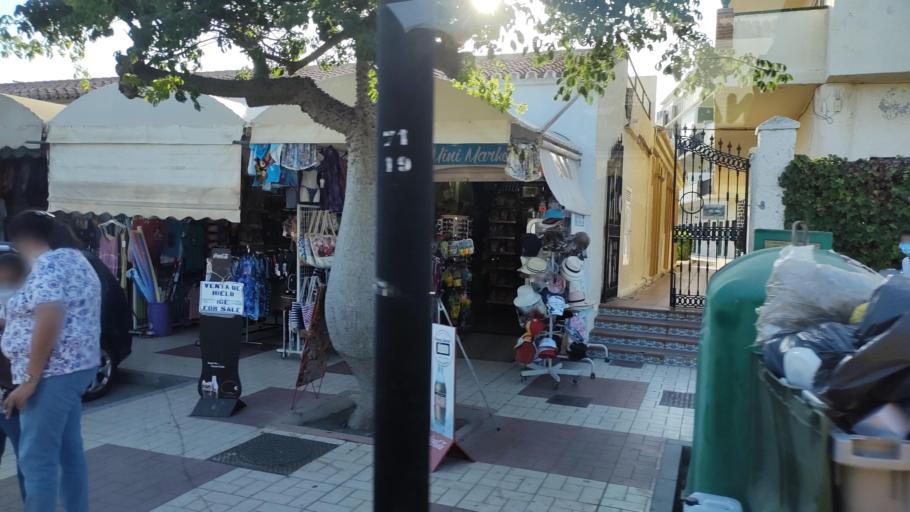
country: ES
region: Andalusia
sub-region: Provincia de Malaga
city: Torremolinos
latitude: 36.6274
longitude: -4.4918
